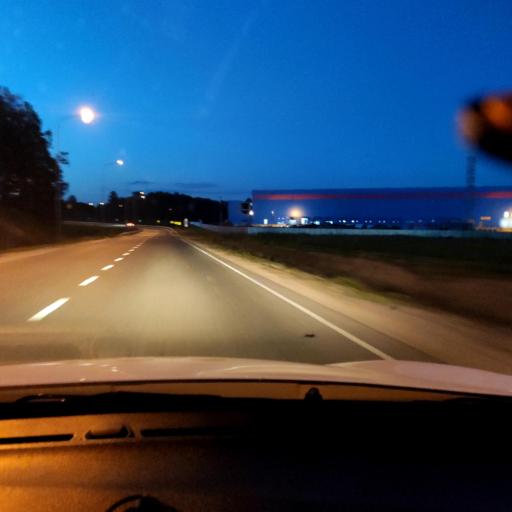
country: RU
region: Tatarstan
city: Osinovo
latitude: 55.8542
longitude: 48.8439
